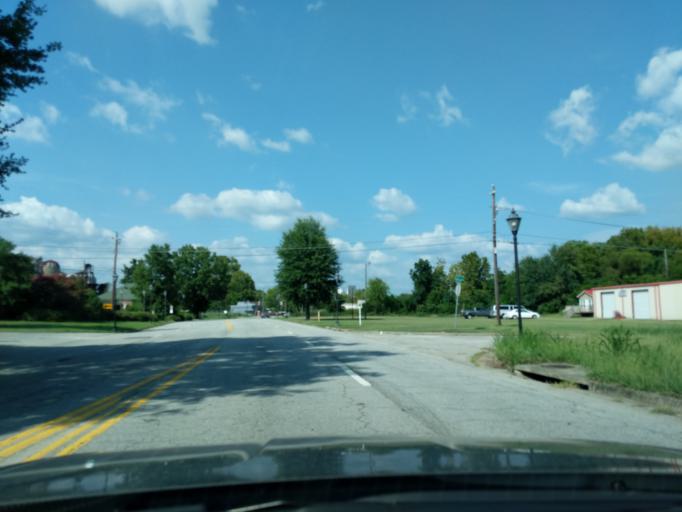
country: US
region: Georgia
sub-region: Richmond County
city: Augusta
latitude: 33.4628
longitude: -81.9692
